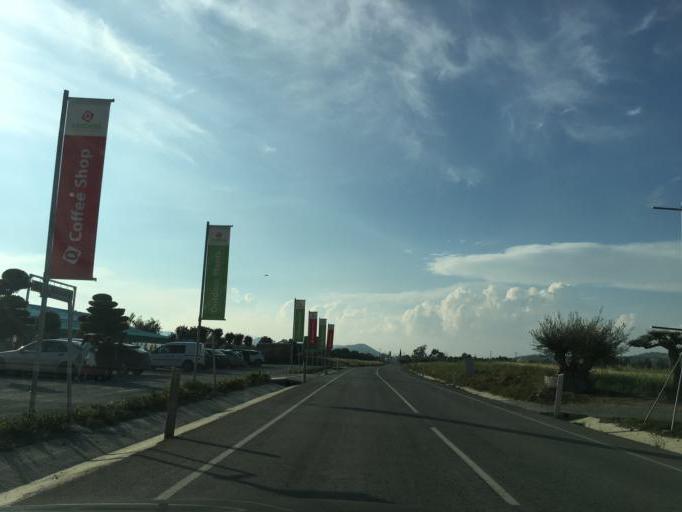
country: CY
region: Larnaka
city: Kofinou
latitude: 34.7468
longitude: 33.3199
